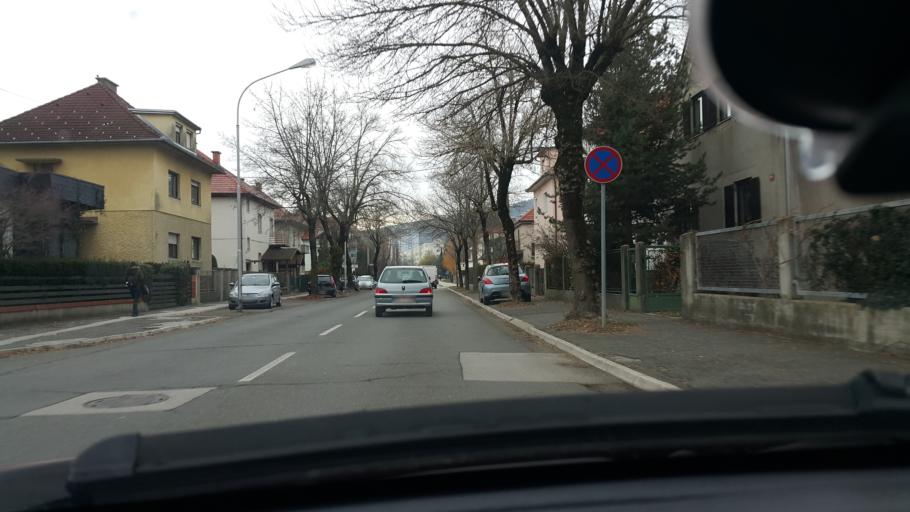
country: SI
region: Maribor
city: Maribor
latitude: 46.5432
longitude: 15.6422
